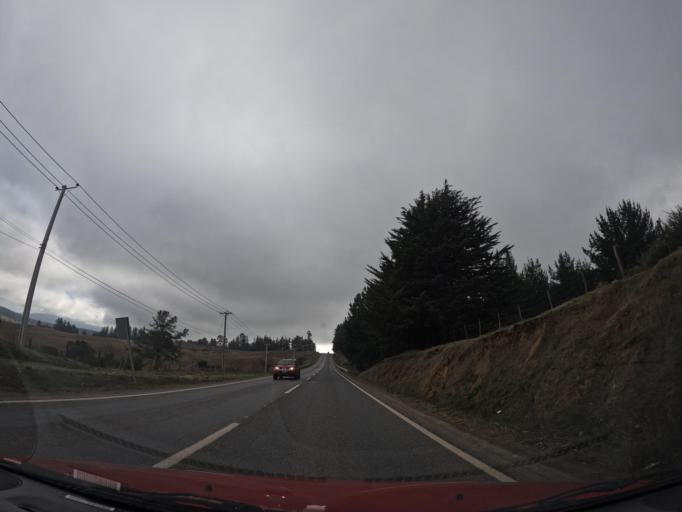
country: CL
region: Maule
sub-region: Provincia de Cauquenes
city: Cauquenes
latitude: -36.2516
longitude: -72.5483
